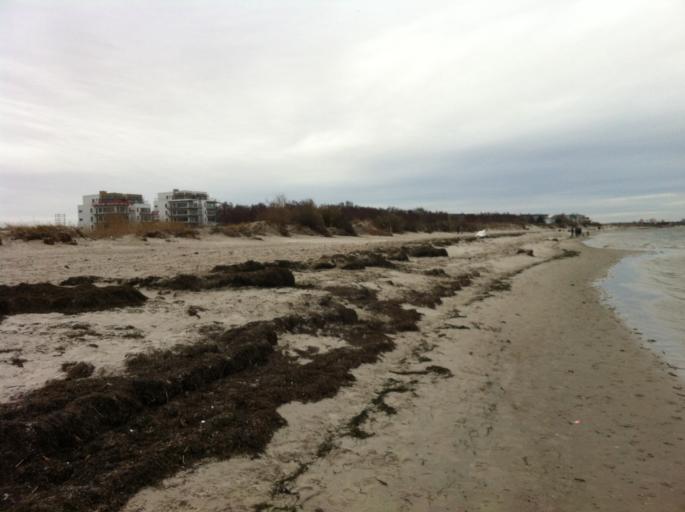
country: SE
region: Skane
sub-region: Lomma Kommun
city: Lomma
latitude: 55.6832
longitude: 13.0571
